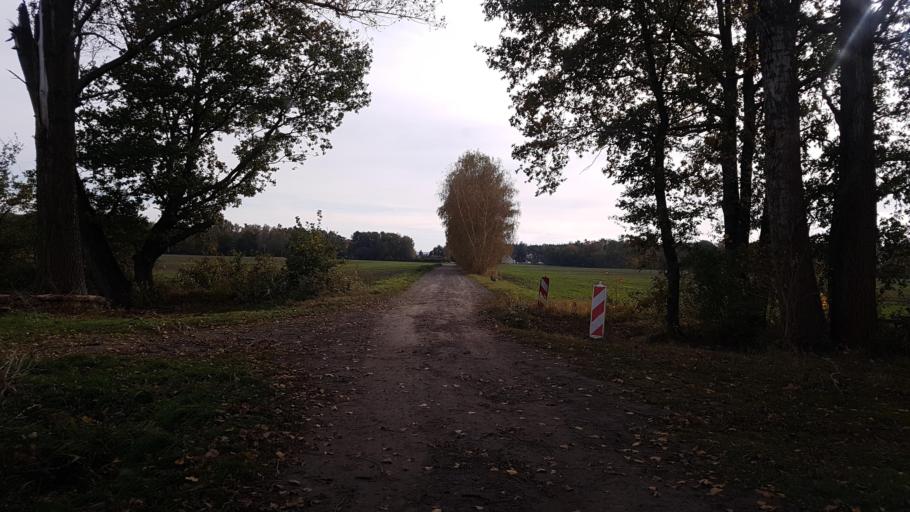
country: DE
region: Brandenburg
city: Schraden
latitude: 51.4463
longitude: 13.6924
